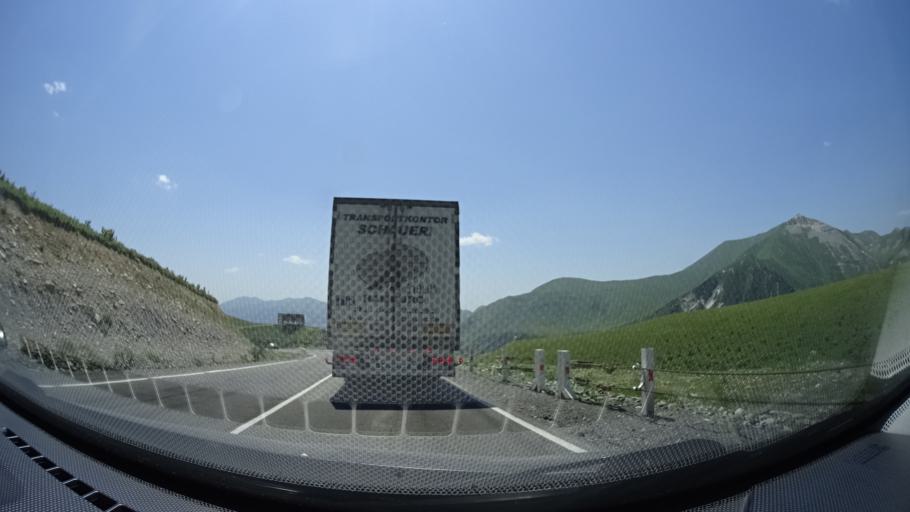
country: GE
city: Gudauri
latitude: 42.4956
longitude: 44.4496
